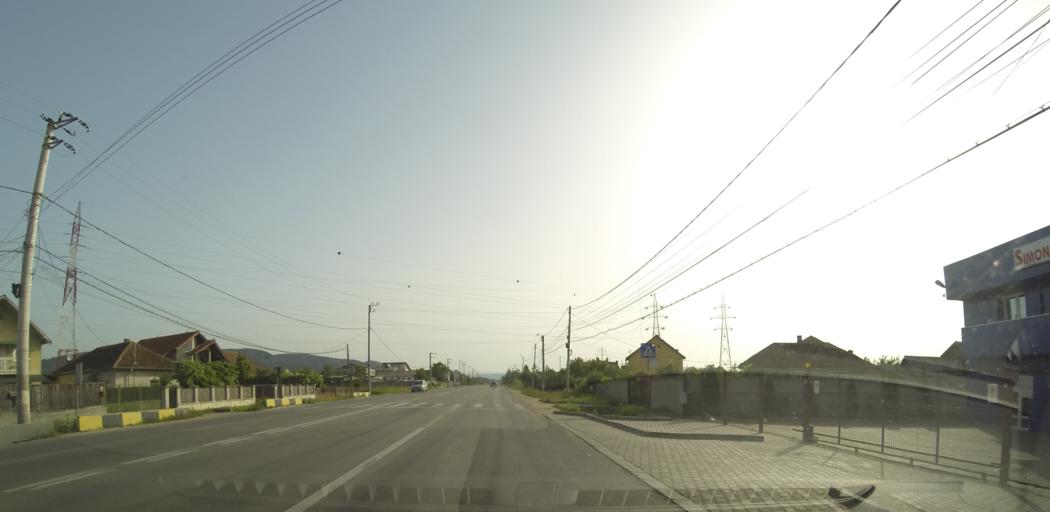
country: RO
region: Valcea
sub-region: Municipiul Ramnicu Valcea
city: Copacelu
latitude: 45.0595
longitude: 24.3339
